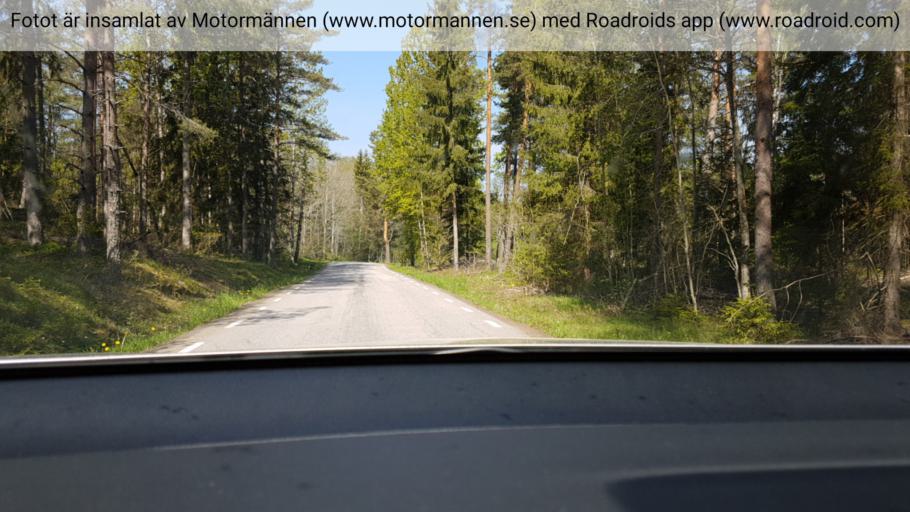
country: SE
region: Kalmar
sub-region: Vasterviks Kommun
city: Forserum
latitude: 57.8654
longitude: 16.4918
